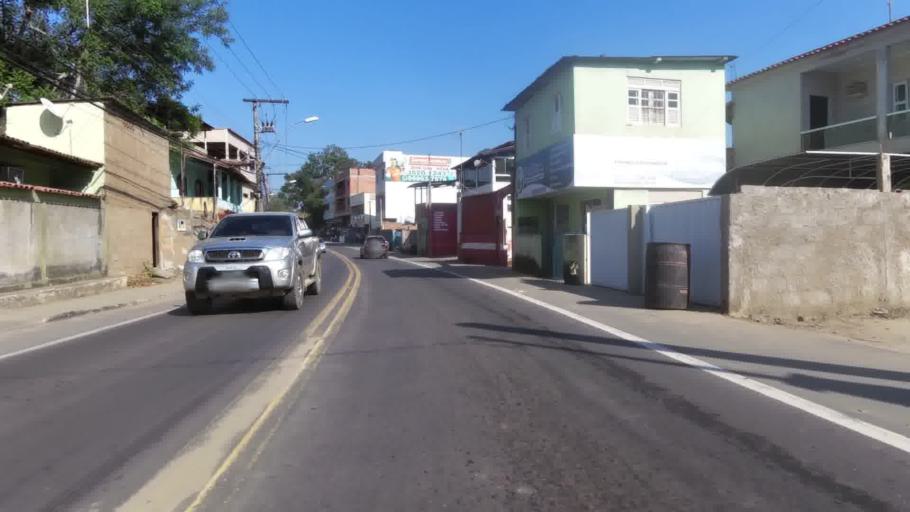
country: BR
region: Espirito Santo
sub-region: Piuma
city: Piuma
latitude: -20.8345
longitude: -40.7262
